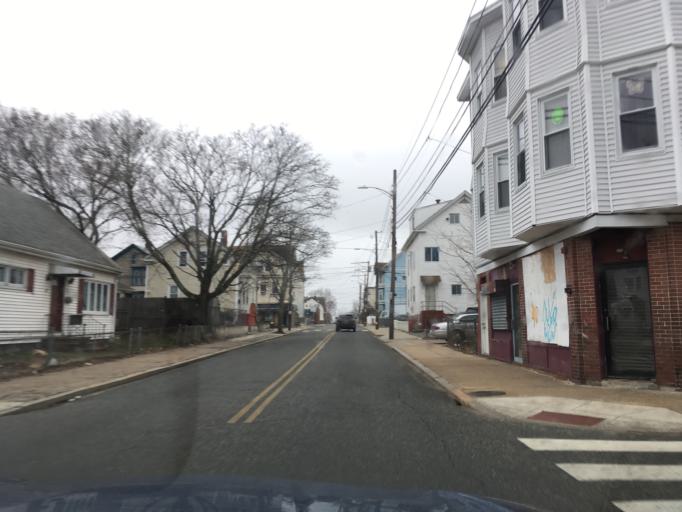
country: US
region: Rhode Island
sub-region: Providence County
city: North Providence
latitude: 41.8281
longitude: -71.4490
